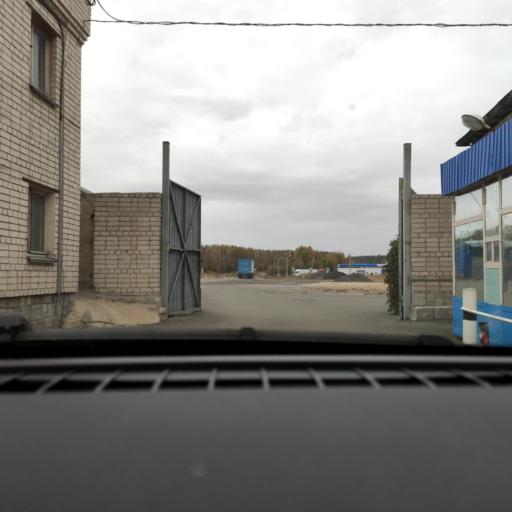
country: RU
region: Voronezj
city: Somovo
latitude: 51.6822
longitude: 39.3007
